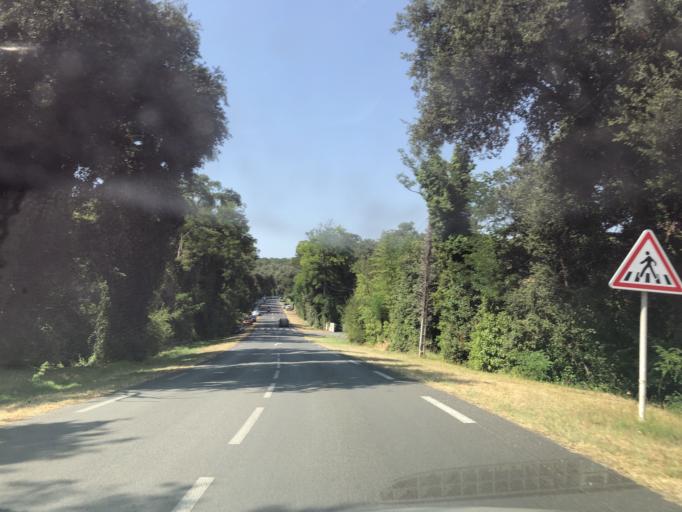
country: FR
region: Poitou-Charentes
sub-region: Departement de la Charente-Maritime
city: Meschers-sur-Gironde
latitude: 45.5649
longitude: -0.9696
